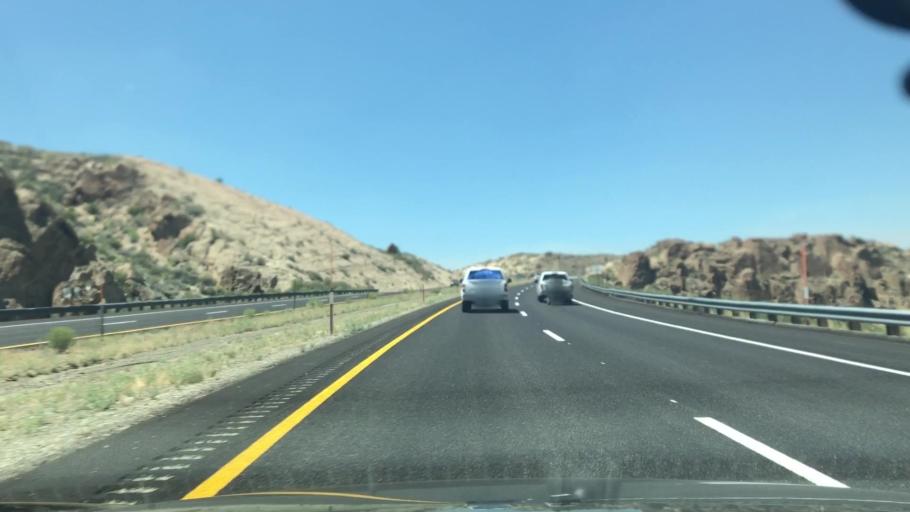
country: US
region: California
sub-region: Mono County
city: Mammoth Lakes
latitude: 37.5723
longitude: -118.7130
